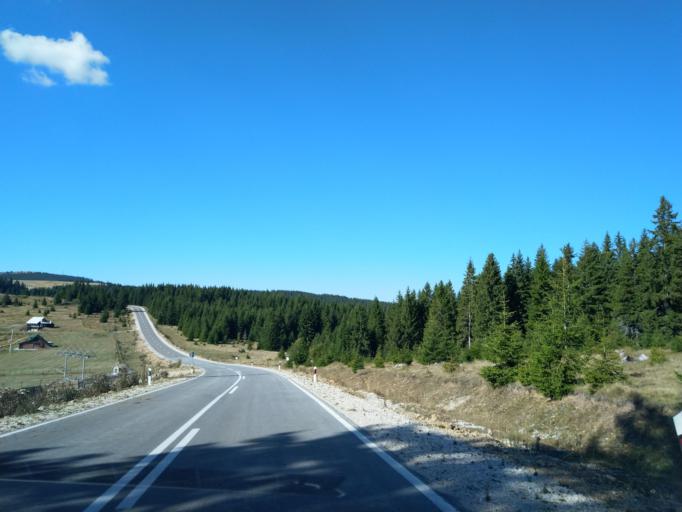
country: RS
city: Sokolovica
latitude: 43.3141
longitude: 20.2948
